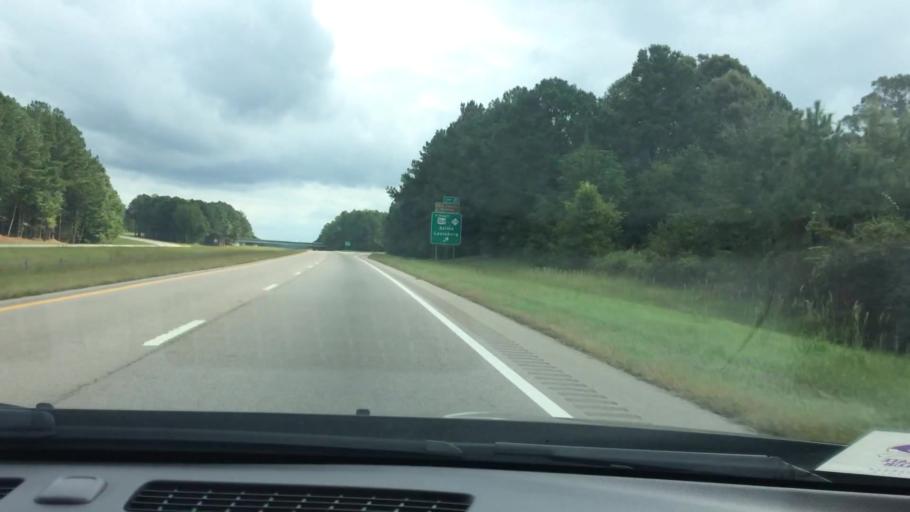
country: US
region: North Carolina
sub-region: Wake County
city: Zebulon
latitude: 35.8219
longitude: -78.2752
